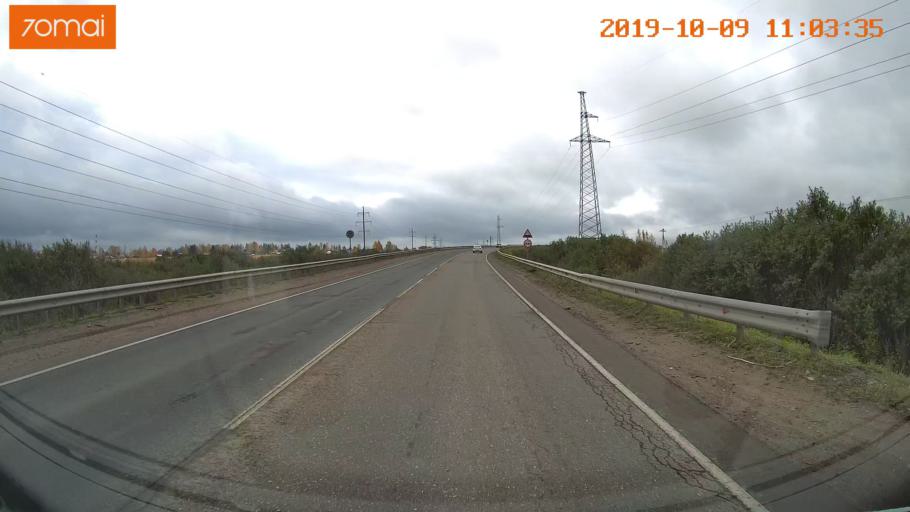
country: RU
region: Vologda
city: Vologda
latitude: 59.2202
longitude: 39.7740
